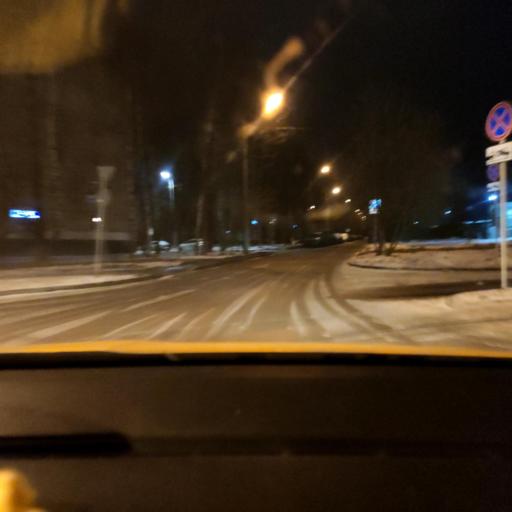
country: RU
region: Moscow
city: Metrogorodok
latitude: 55.8276
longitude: 37.7647
